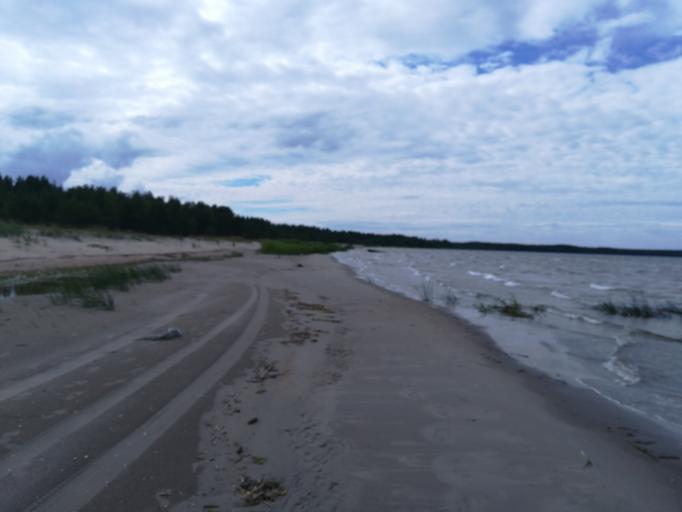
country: RU
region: Leningrad
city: Ust'-Luga
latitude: 59.6786
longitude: 28.2444
